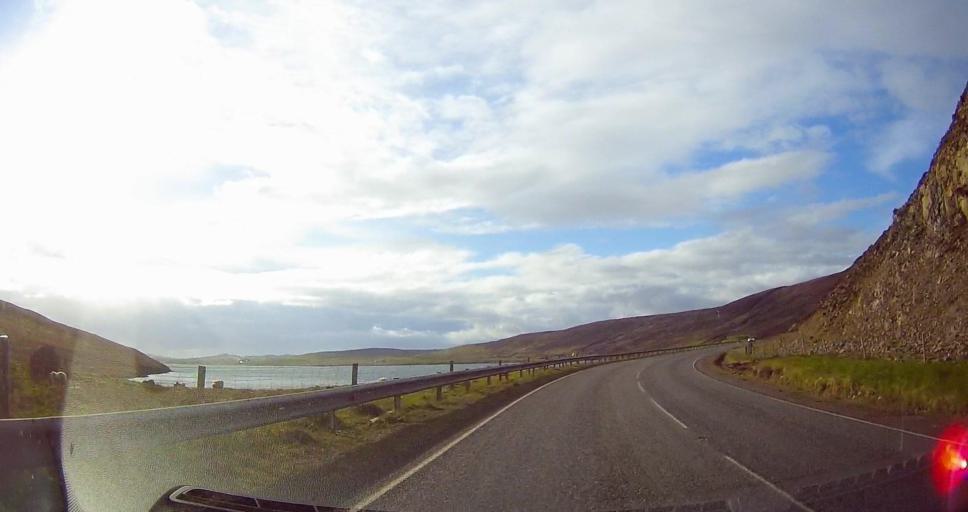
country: GB
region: Scotland
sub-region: Shetland Islands
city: Lerwick
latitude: 60.3572
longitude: -1.2826
